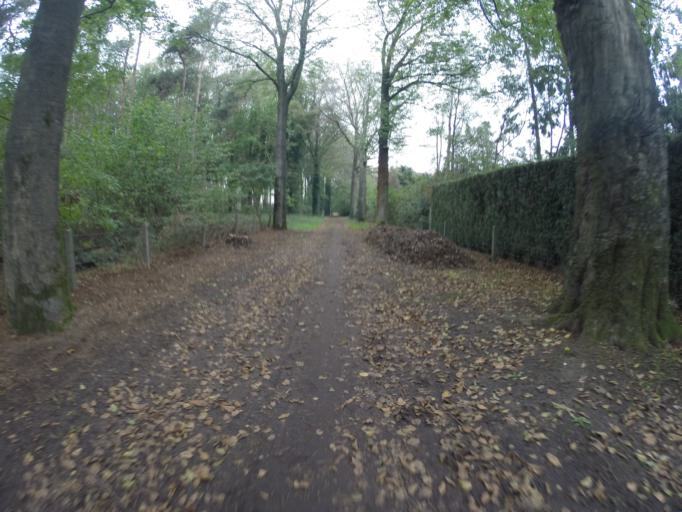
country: BE
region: Flanders
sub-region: Provincie West-Vlaanderen
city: Beernem
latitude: 51.0844
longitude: 3.3440
